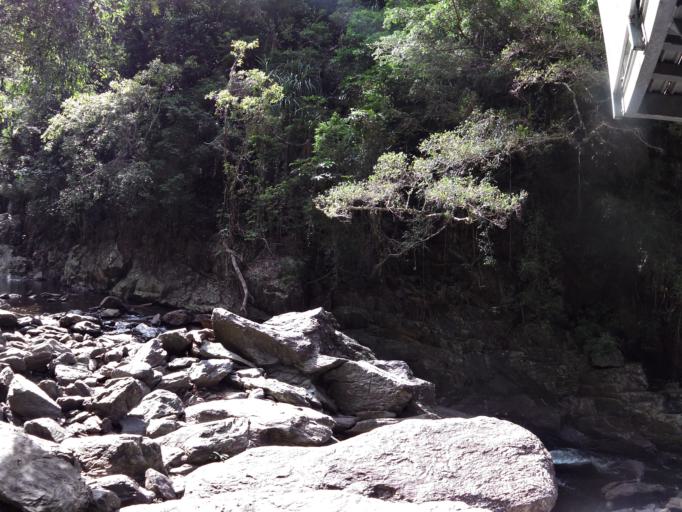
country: AU
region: Queensland
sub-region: Cairns
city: Woree
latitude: -16.9638
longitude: 145.6709
